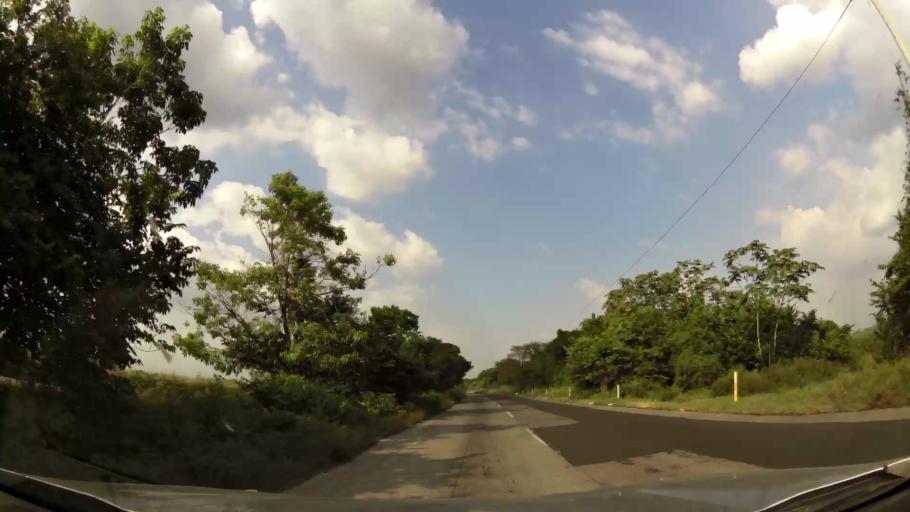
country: GT
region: Escuintla
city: Puerto San Jose
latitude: 14.0581
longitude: -90.7759
